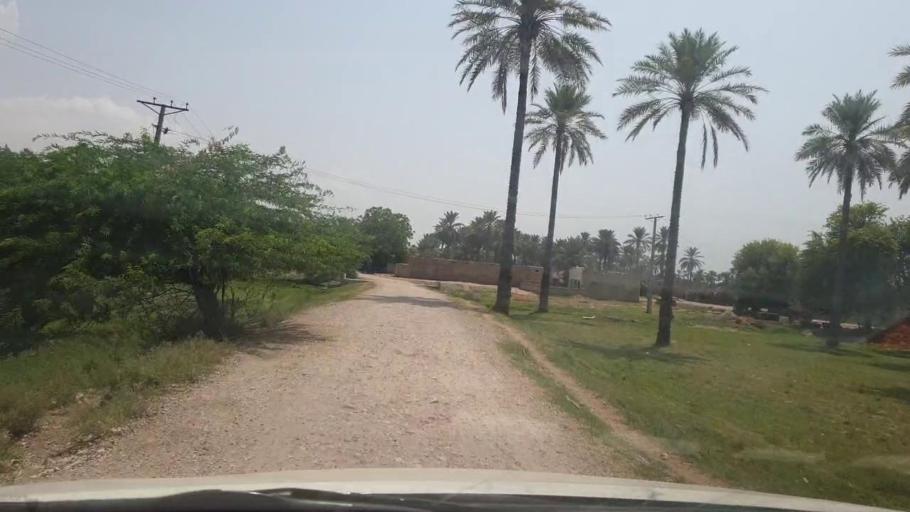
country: PK
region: Sindh
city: Khairpur
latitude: 27.5525
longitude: 68.8277
